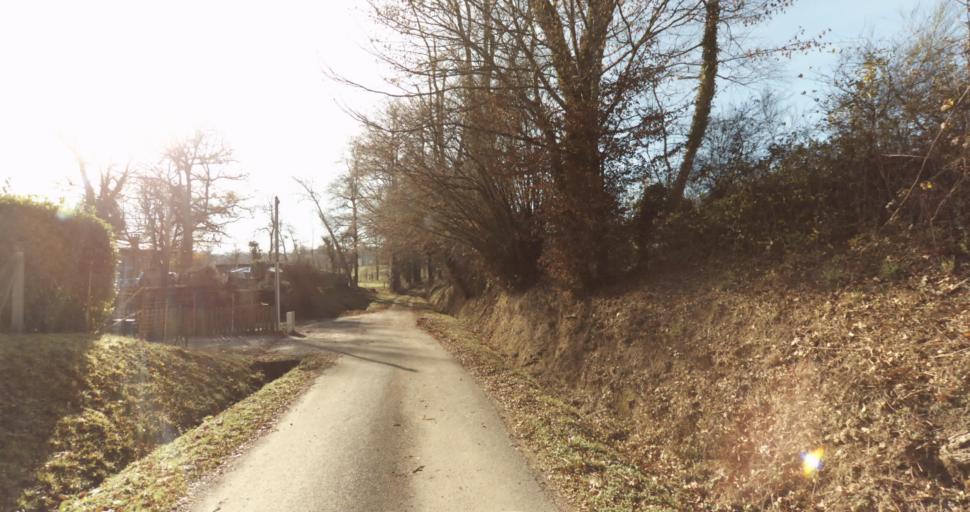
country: FR
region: Limousin
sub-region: Departement de la Haute-Vienne
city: Aixe-sur-Vienne
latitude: 45.7768
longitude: 1.1282
